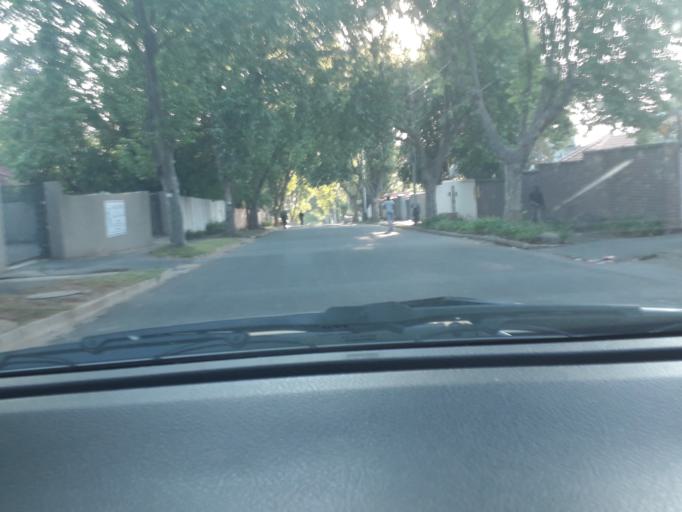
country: ZA
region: Gauteng
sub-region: City of Johannesburg Metropolitan Municipality
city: Johannesburg
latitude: -26.1245
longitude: 28.0789
